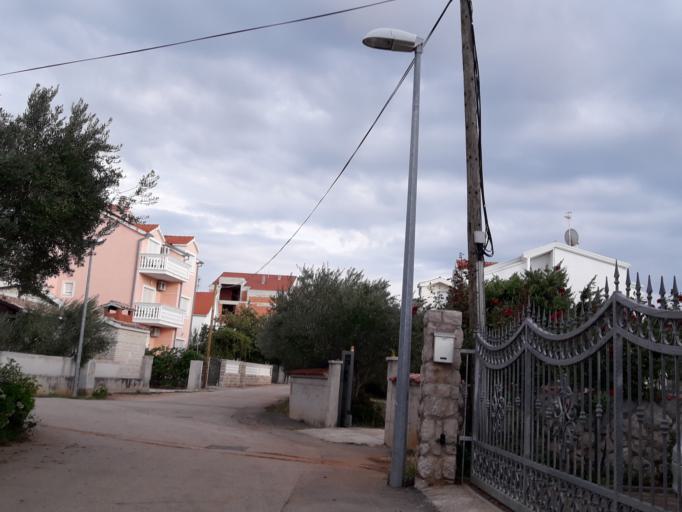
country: HR
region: Sibensko-Kniniska
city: Vodice
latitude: 43.7476
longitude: 15.7985
